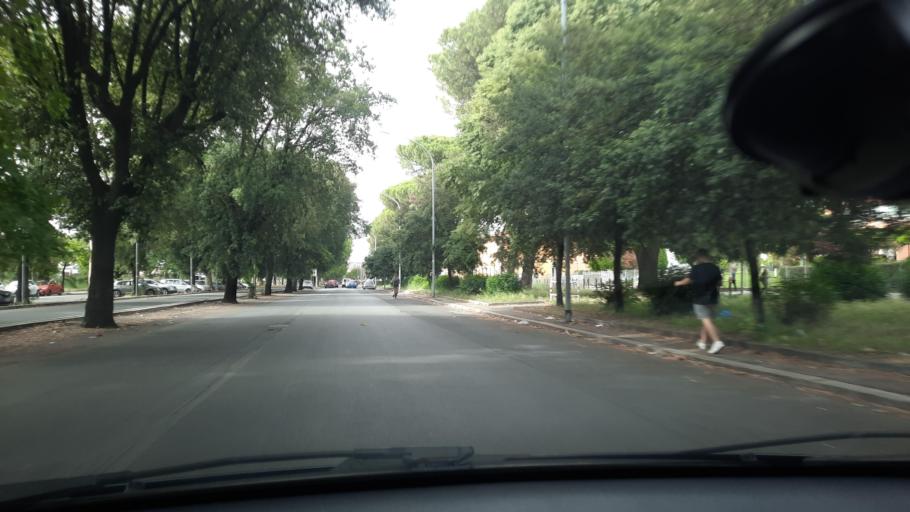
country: IT
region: Latium
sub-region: Citta metropolitana di Roma Capitale
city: Rome
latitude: 41.8612
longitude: 12.4784
